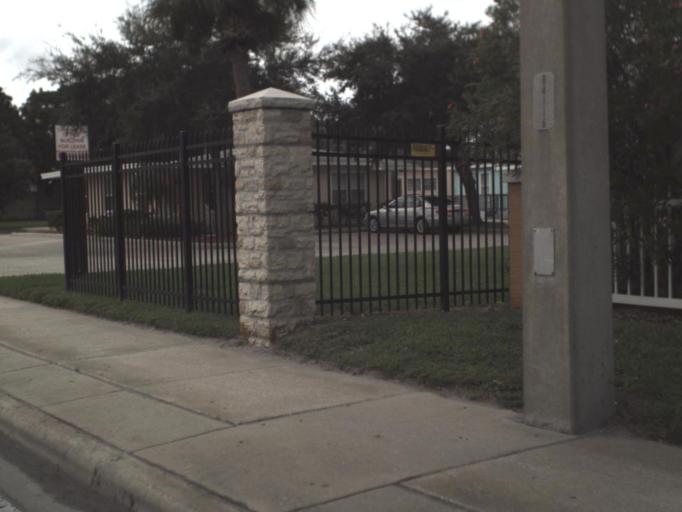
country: US
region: Florida
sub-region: Manatee County
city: South Bradenton
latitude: 27.4699
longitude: -82.5755
